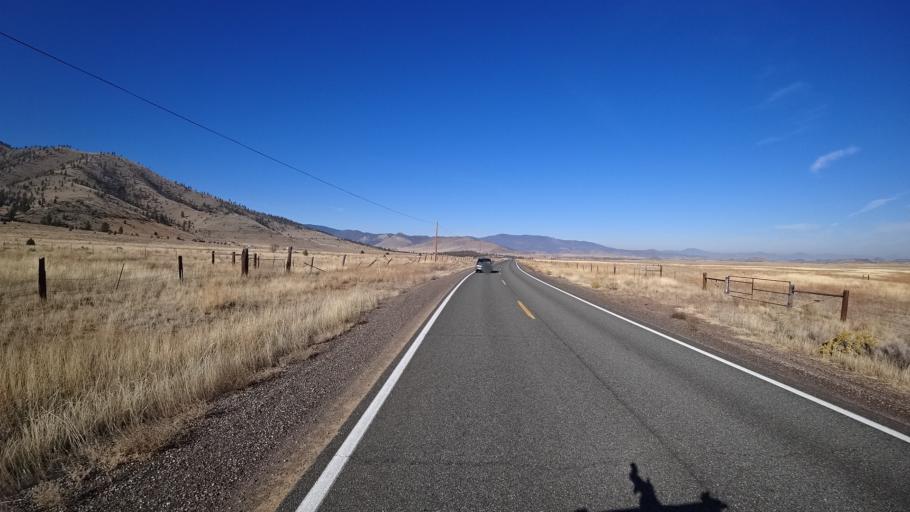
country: US
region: California
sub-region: Siskiyou County
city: Weed
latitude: 41.4794
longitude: -122.4926
